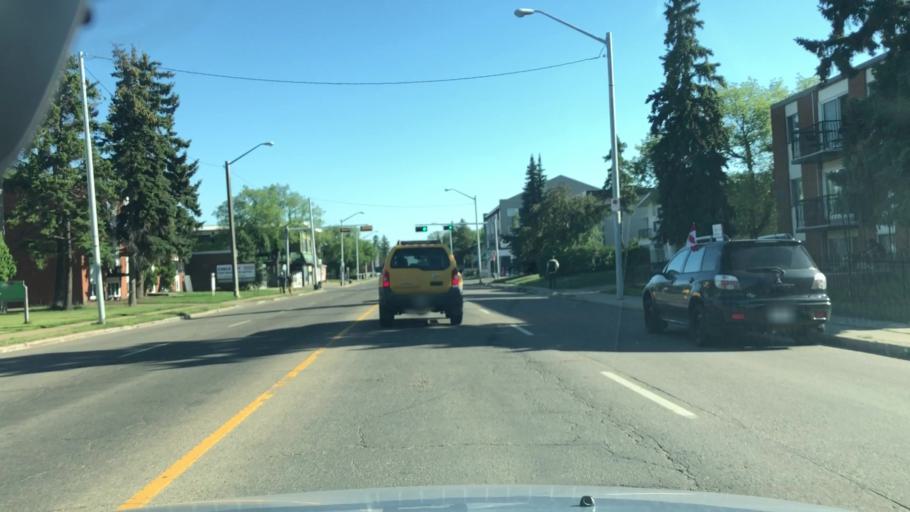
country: CA
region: Alberta
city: Edmonton
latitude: 53.5661
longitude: -113.5360
